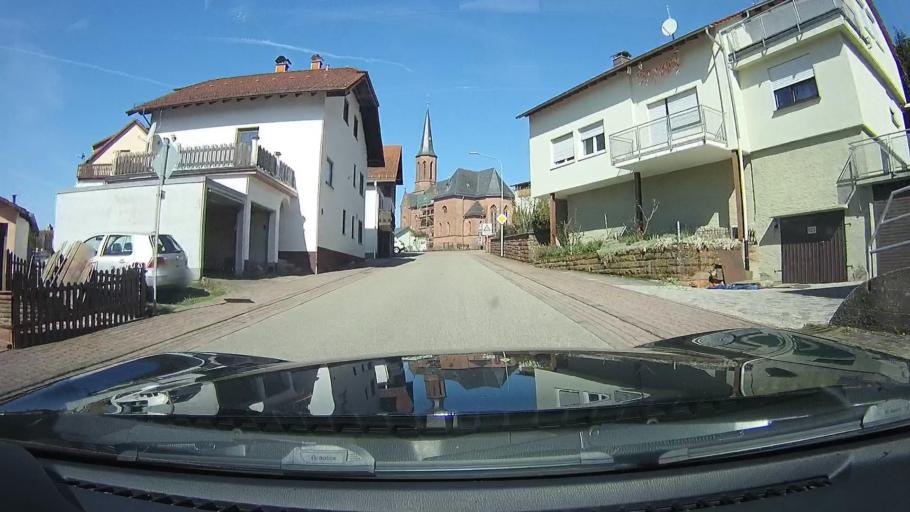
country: DE
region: Hesse
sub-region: Regierungsbezirk Darmstadt
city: Rothenberg
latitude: 49.4980
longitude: 8.9196
